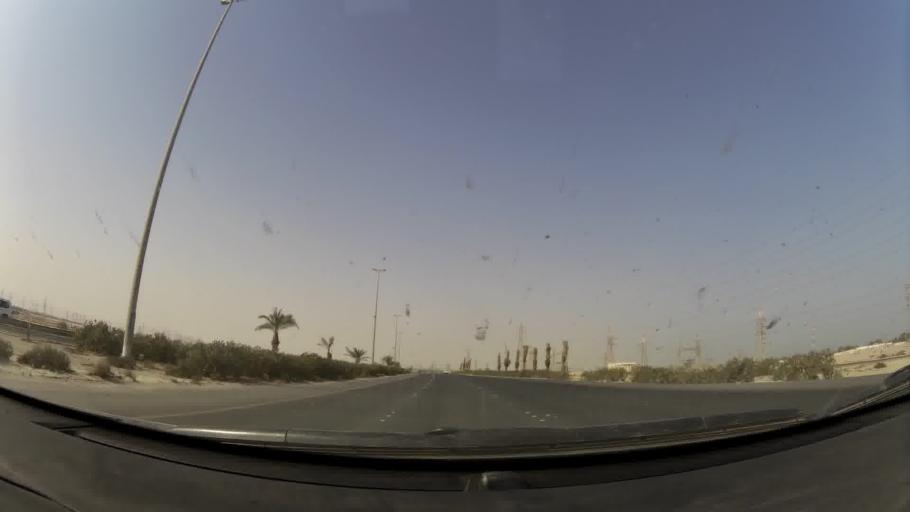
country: KW
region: Al Ahmadi
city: Al Fahahil
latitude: 28.9316
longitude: 48.1959
